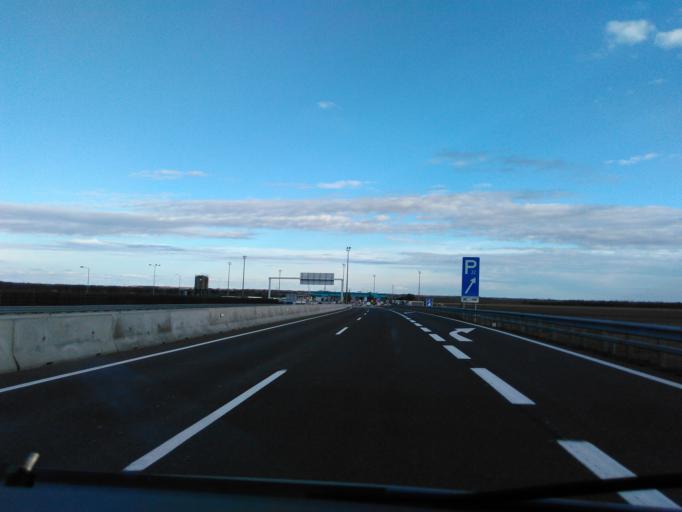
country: AT
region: Burgenland
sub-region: Politischer Bezirk Neusiedl am See
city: Kittsee
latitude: 48.0732
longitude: 17.0648
